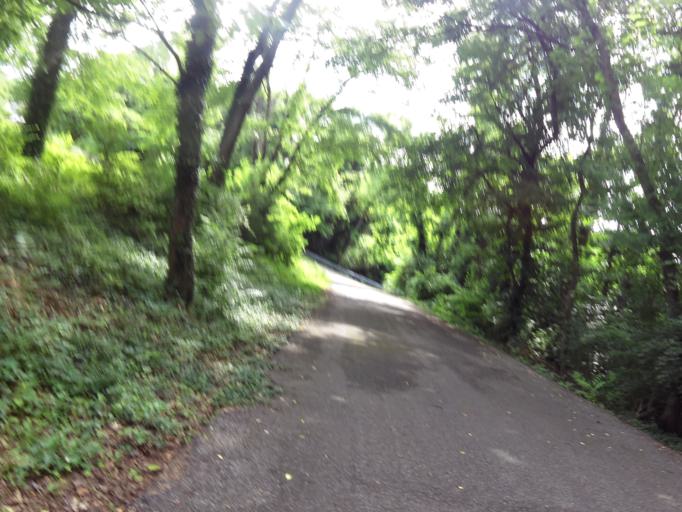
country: US
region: Tennessee
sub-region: Knox County
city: Knoxville
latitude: 35.9579
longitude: -83.9034
